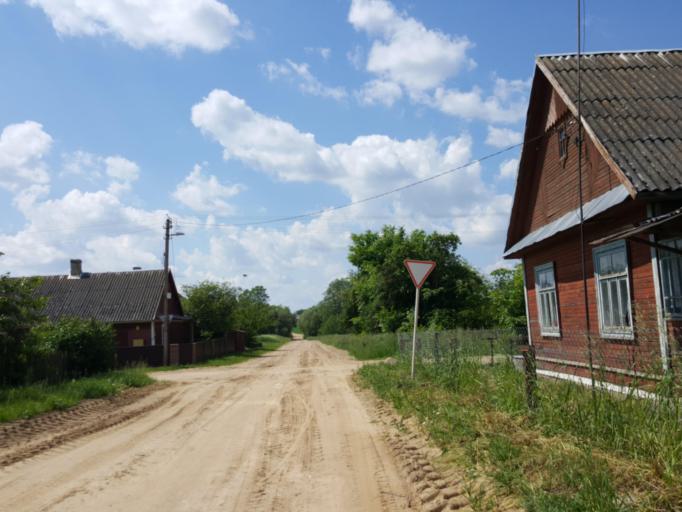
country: BY
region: Brest
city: Kamyanyets
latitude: 52.3979
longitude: 23.7584
